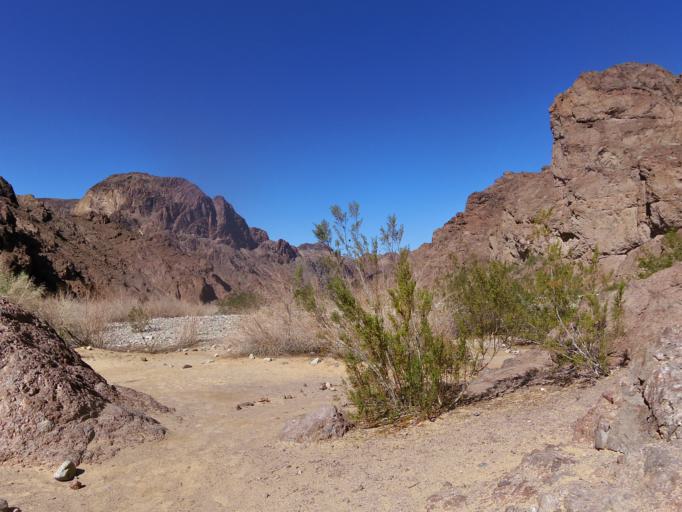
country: US
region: Nevada
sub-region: Clark County
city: Boulder City
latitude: 35.9628
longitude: -114.7291
